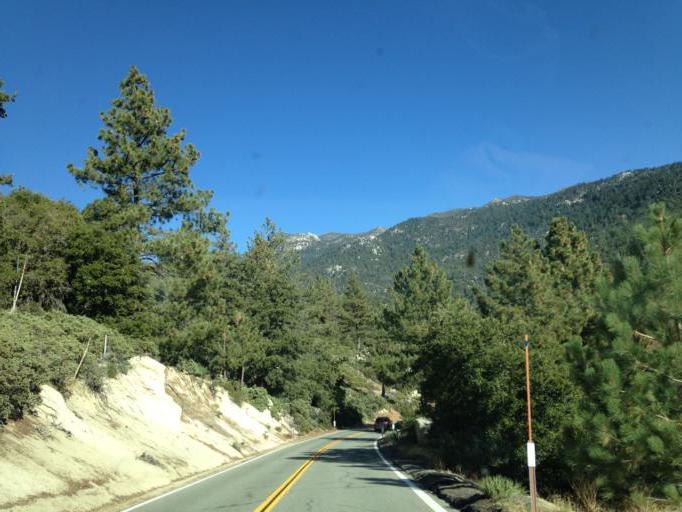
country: US
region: California
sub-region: Riverside County
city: Idyllwild-Pine Cove
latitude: 33.7963
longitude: -116.7534
